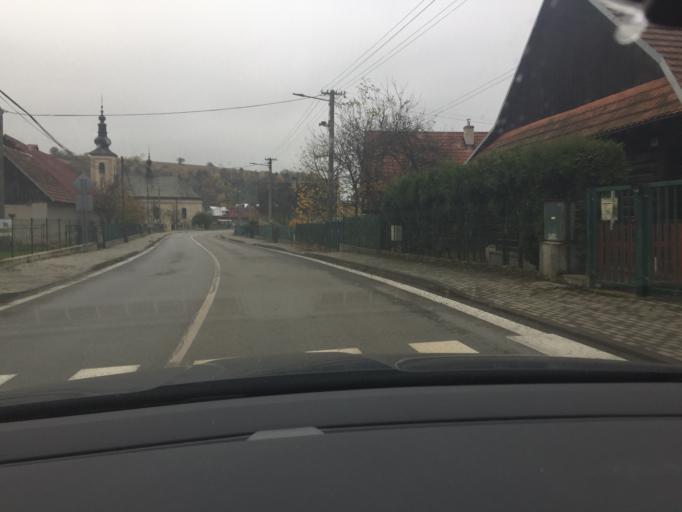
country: PL
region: Lesser Poland Voivodeship
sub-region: Powiat nowosadecki
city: Tylicz
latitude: 49.3202
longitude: 21.1071
